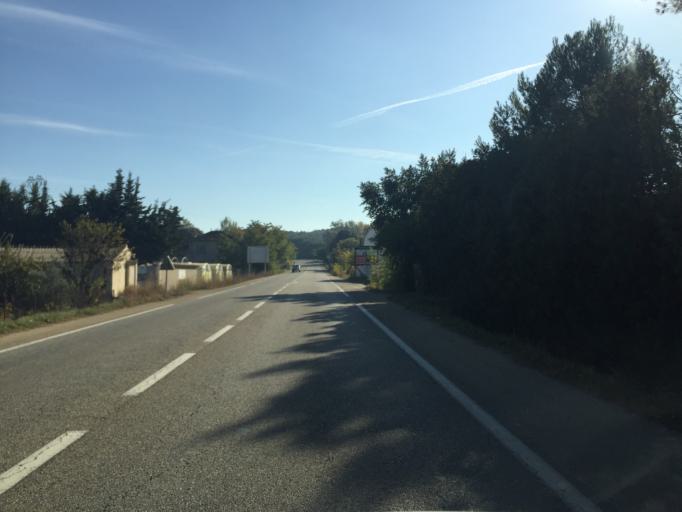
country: FR
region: Provence-Alpes-Cote d'Azur
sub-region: Departement du Vaucluse
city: Cavaillon
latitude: 43.8174
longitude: 5.0164
